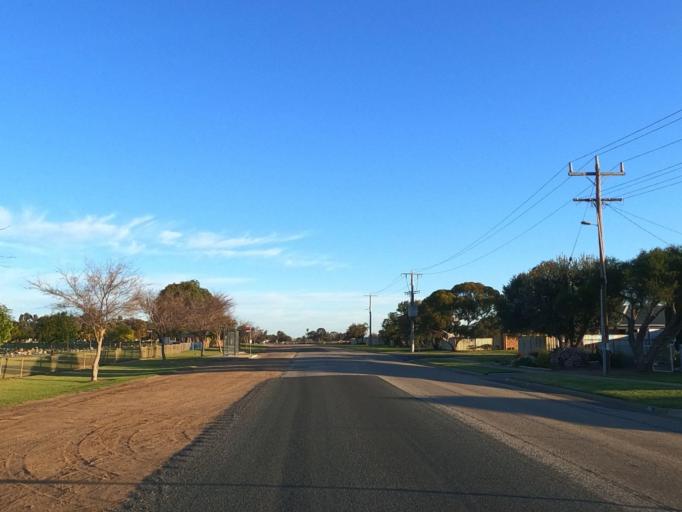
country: AU
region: Victoria
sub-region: Swan Hill
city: Swan Hill
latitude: -35.3531
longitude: 143.5532
